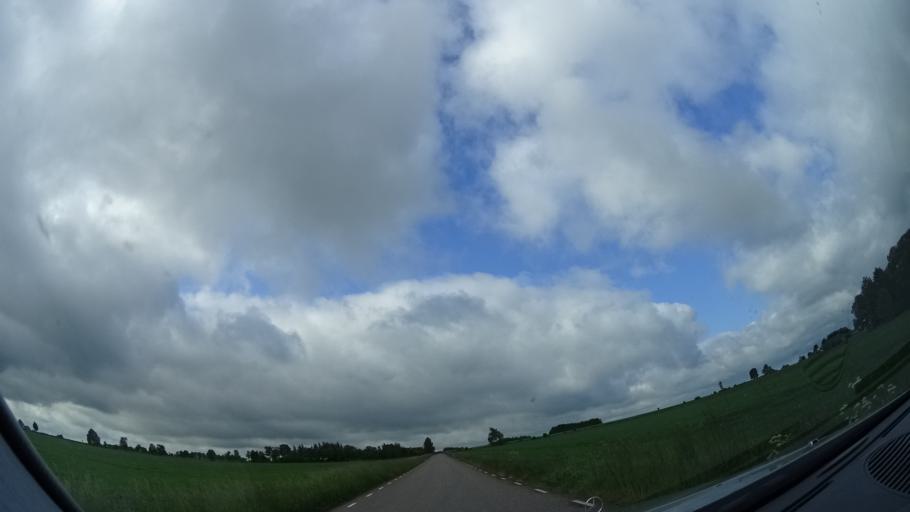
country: SE
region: Skane
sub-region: Hoors Kommun
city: Loberod
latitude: 55.8273
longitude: 13.4510
